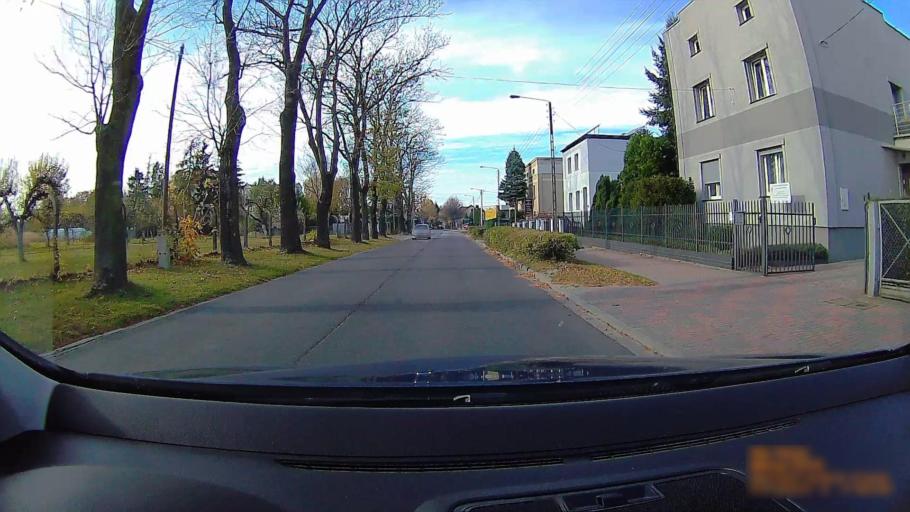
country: PL
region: Greater Poland Voivodeship
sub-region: Powiat ostrzeszowski
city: Ostrzeszow
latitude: 51.4322
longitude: 17.9341
